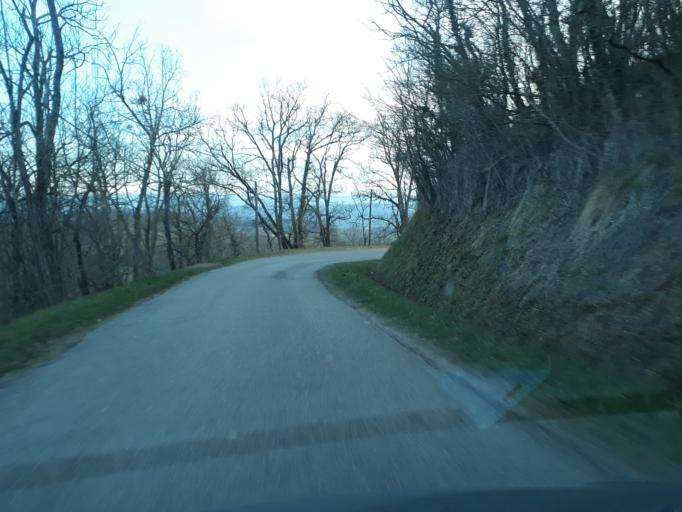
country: FR
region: Midi-Pyrenees
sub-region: Departement de la Haute-Garonne
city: Montesquieu-Volvestre
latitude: 43.1733
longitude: 1.3223
